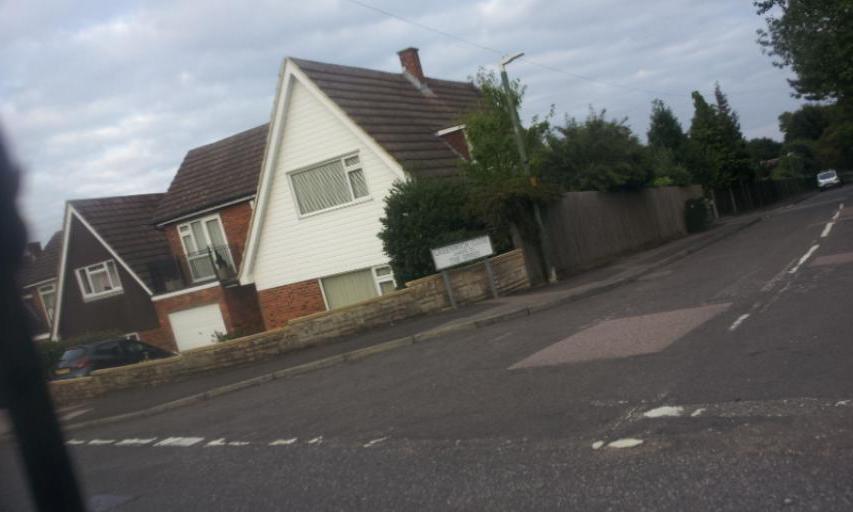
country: GB
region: England
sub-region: Kent
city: Maidstone
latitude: 51.2758
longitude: 0.5031
